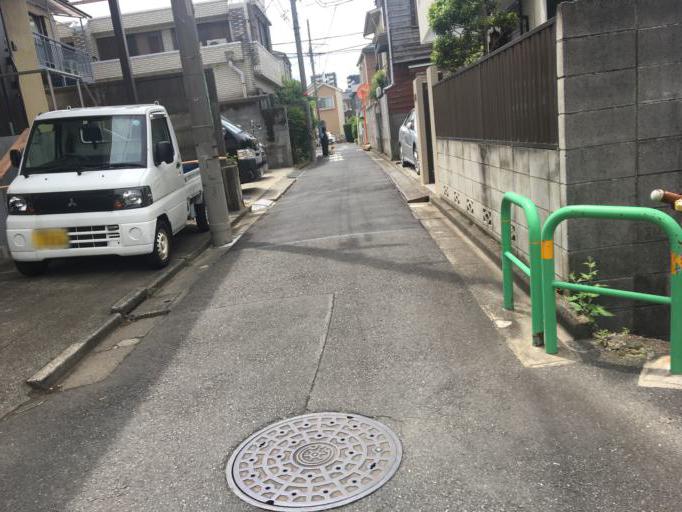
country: JP
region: Saitama
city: Wako
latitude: 35.7421
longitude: 139.6595
